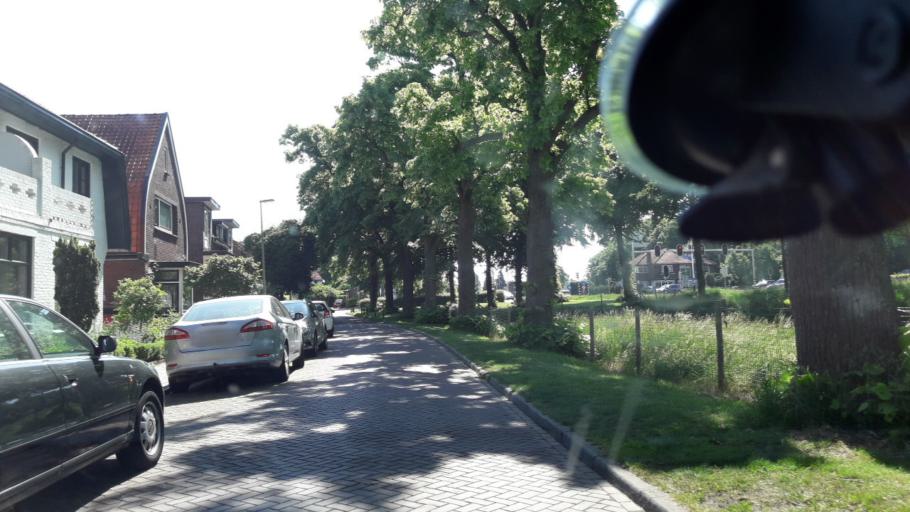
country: NL
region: Overijssel
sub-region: Gemeente Deventer
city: Deventer
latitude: 52.2469
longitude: 6.1418
